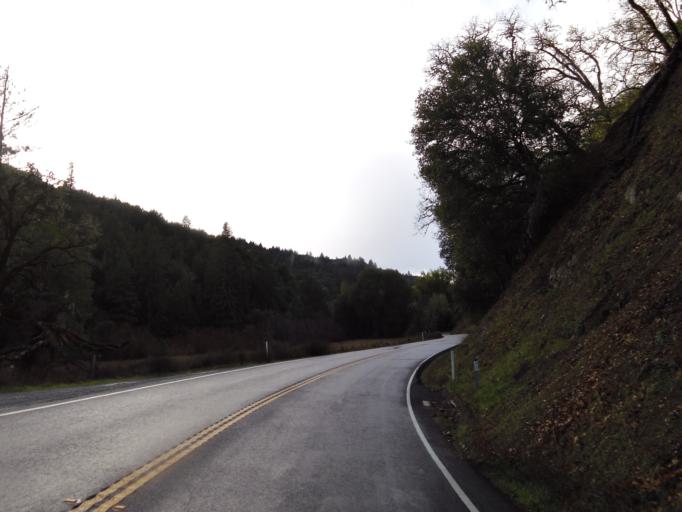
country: US
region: California
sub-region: Sonoma County
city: Cloverdale
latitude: 38.8852
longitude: -123.1575
